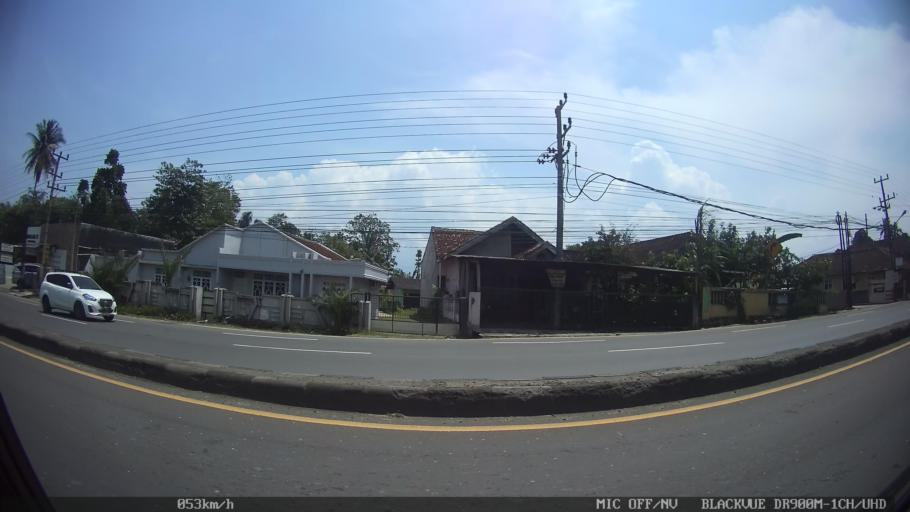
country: ID
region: Lampung
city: Kedaton
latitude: -5.3578
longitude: 105.2218
